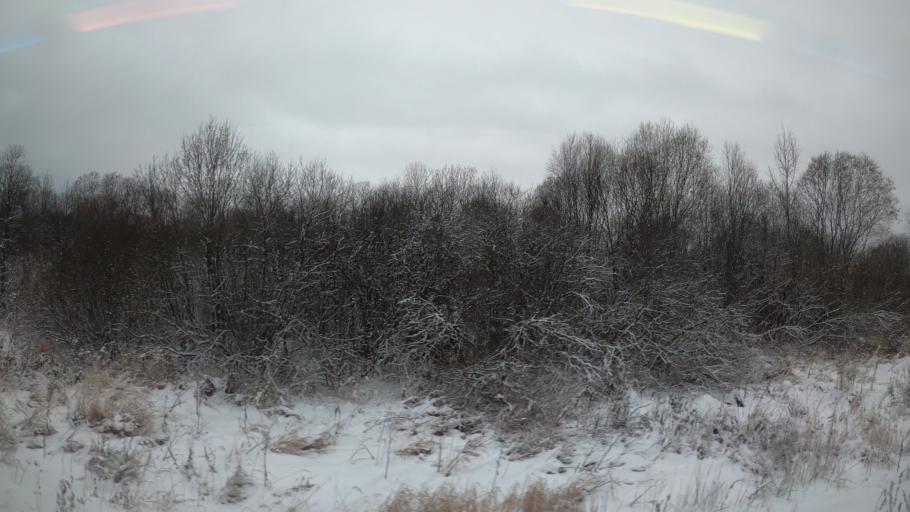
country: RU
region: Jaroslavl
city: Pereslavl'-Zalesskiy
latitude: 56.7089
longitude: 38.9112
